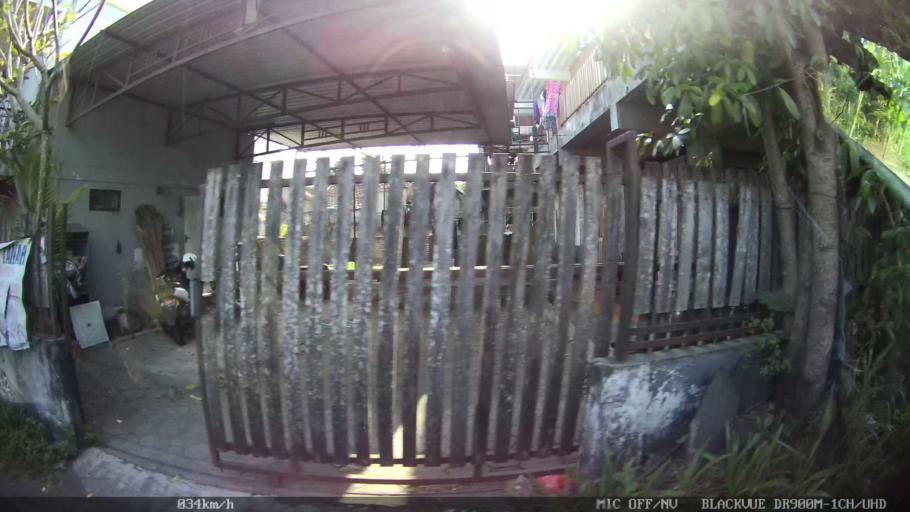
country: ID
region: Daerah Istimewa Yogyakarta
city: Kasihan
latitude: -7.8400
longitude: 110.3440
